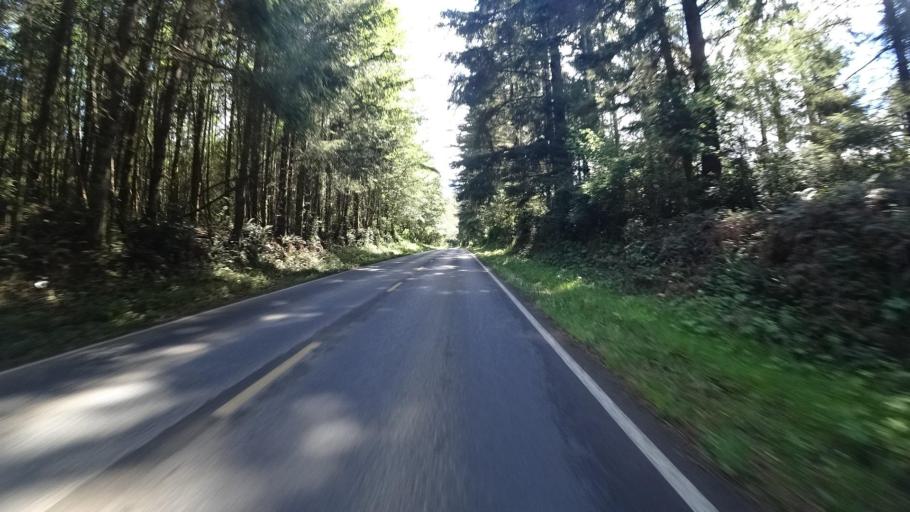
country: US
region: California
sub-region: Humboldt County
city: McKinleyville
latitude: 40.9552
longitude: -124.0759
